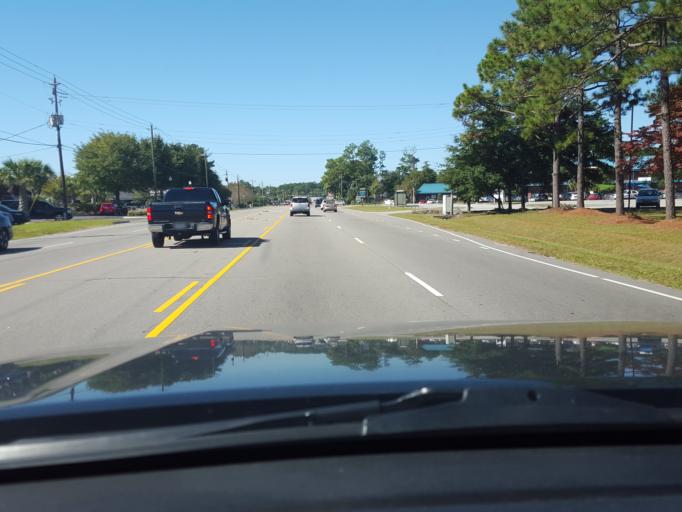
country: US
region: North Carolina
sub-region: New Hanover County
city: Seagate
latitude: 34.2083
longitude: -77.8586
